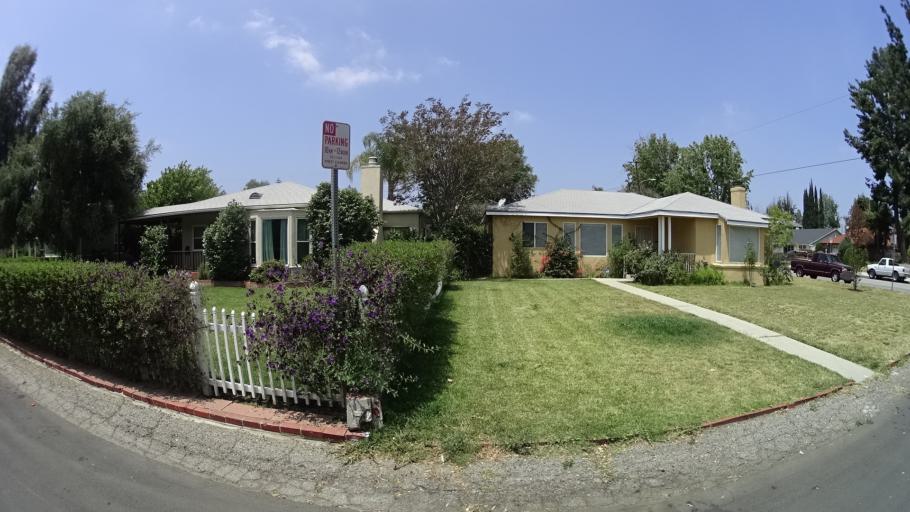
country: US
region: California
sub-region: Los Angeles County
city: Van Nuys
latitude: 34.1919
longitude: -118.4587
